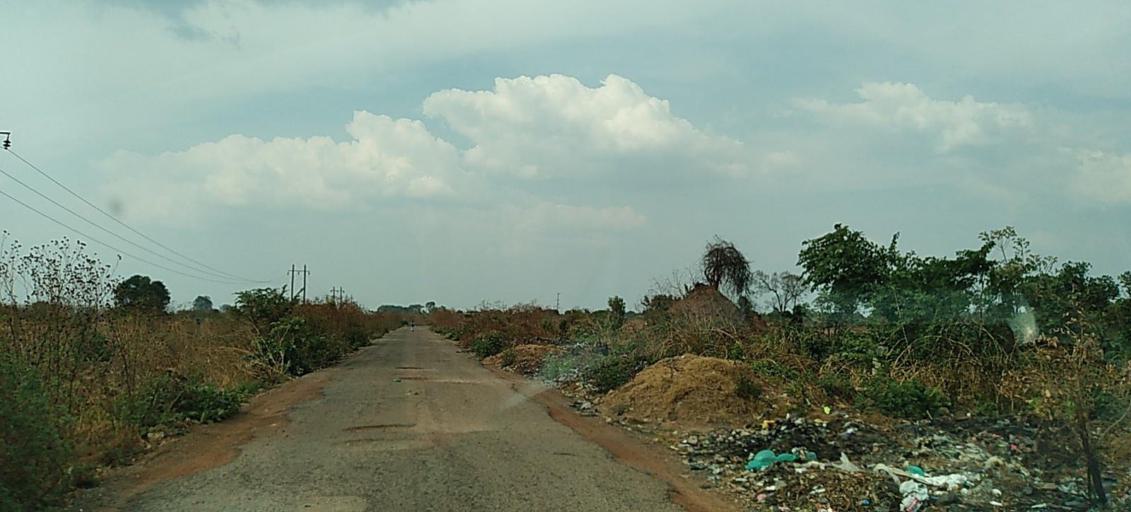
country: ZM
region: Copperbelt
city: Chililabombwe
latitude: -12.3767
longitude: 27.8133
